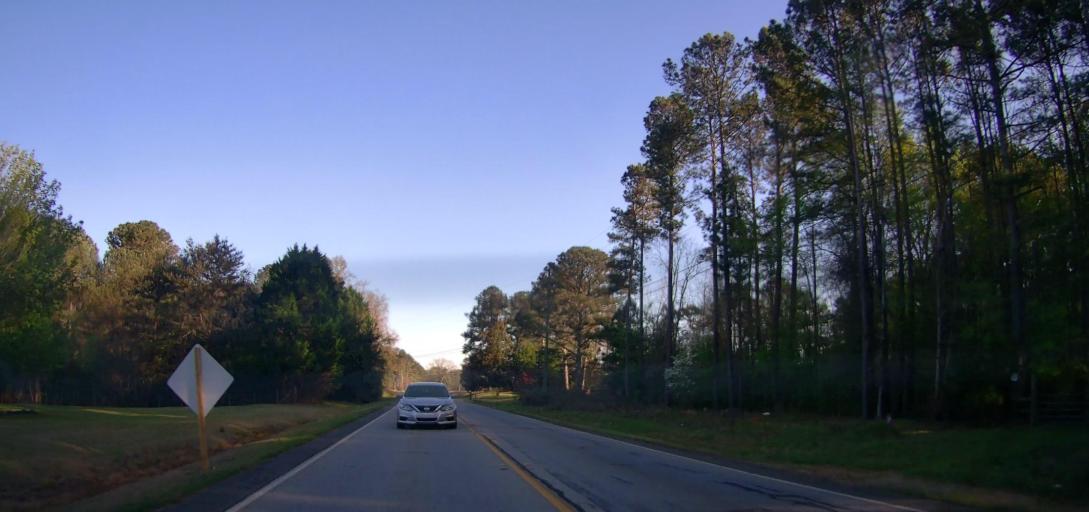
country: US
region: Georgia
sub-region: Newton County
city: Oakwood
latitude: 33.4609
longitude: -83.9063
